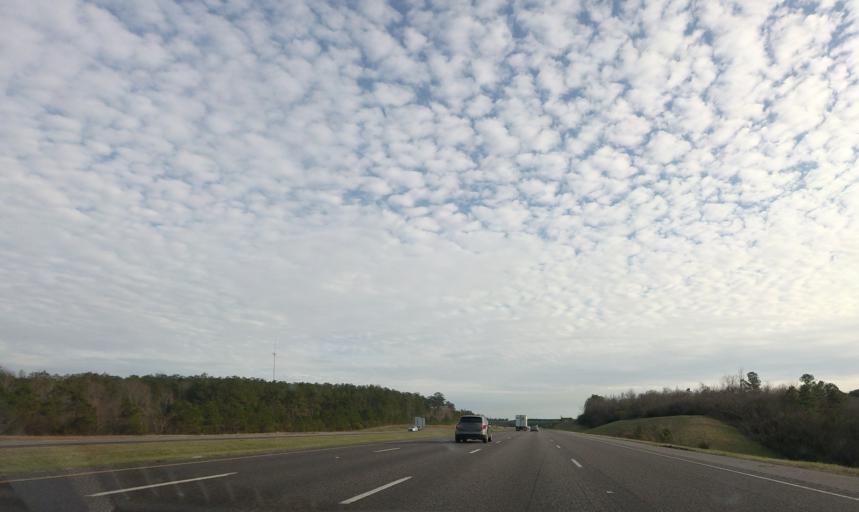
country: US
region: Alabama
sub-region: Walker County
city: Dora
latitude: 33.6752
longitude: -87.0787
